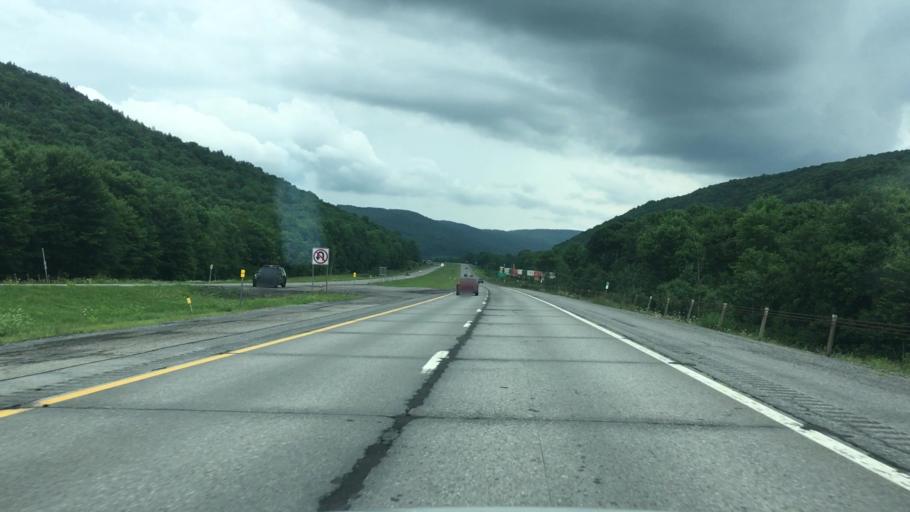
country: US
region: New York
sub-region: Otsego County
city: Worcester
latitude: 42.6415
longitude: -74.6501
